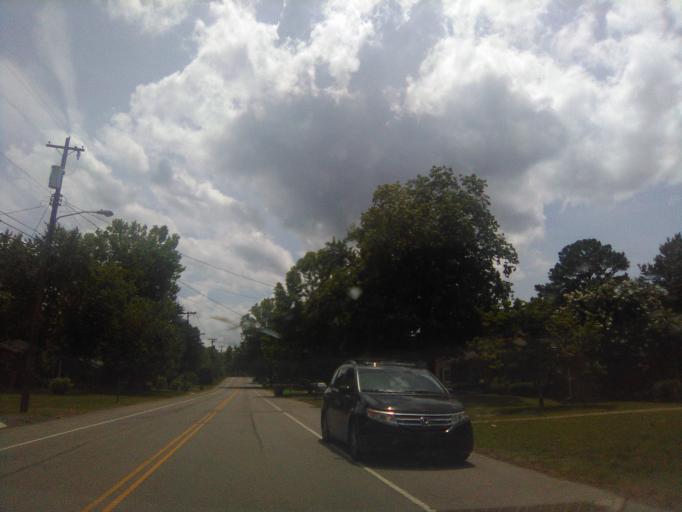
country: US
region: Tennessee
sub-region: Davidson County
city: Belle Meade
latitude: 36.0926
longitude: -86.8789
